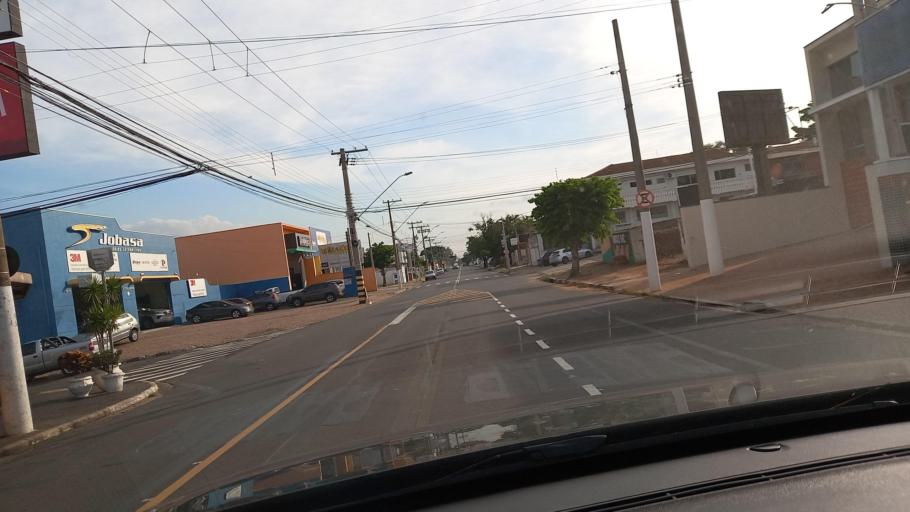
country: BR
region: Sao Paulo
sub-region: Mogi-Mirim
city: Mogi Mirim
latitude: -22.4419
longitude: -46.9687
